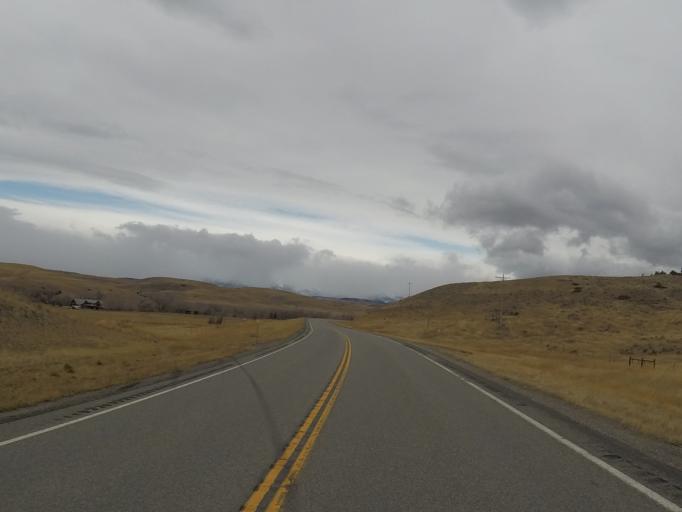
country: US
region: Montana
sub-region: Sweet Grass County
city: Big Timber
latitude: 45.8995
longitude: -109.9679
